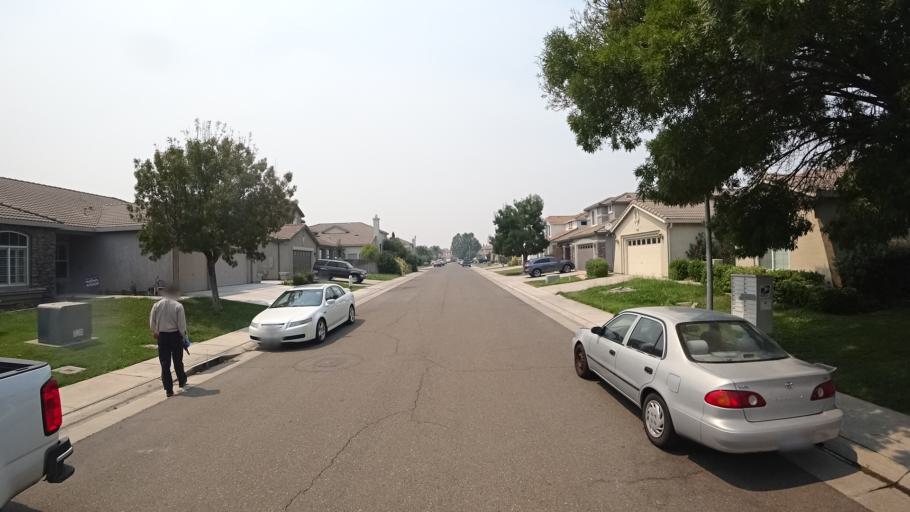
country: US
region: California
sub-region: Sacramento County
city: Laguna
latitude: 38.4011
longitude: -121.4266
